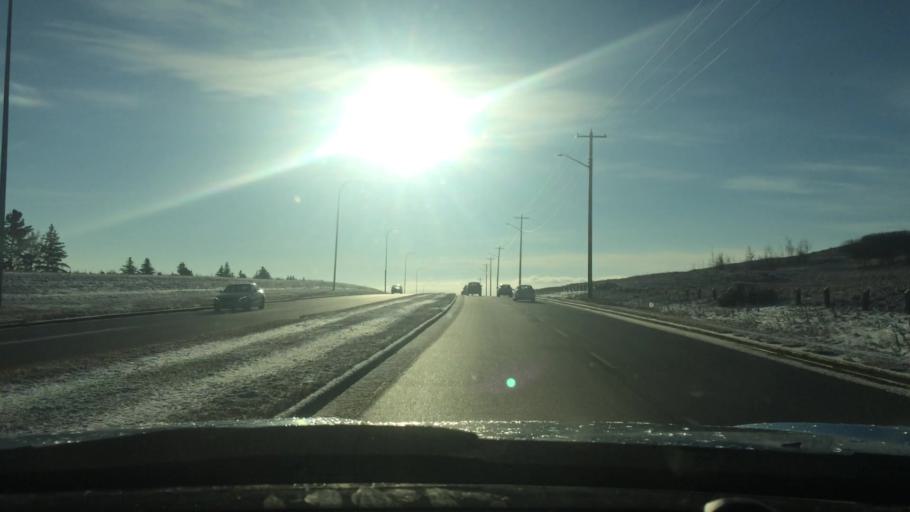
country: CA
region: Alberta
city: Calgary
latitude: 51.1220
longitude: -114.0928
